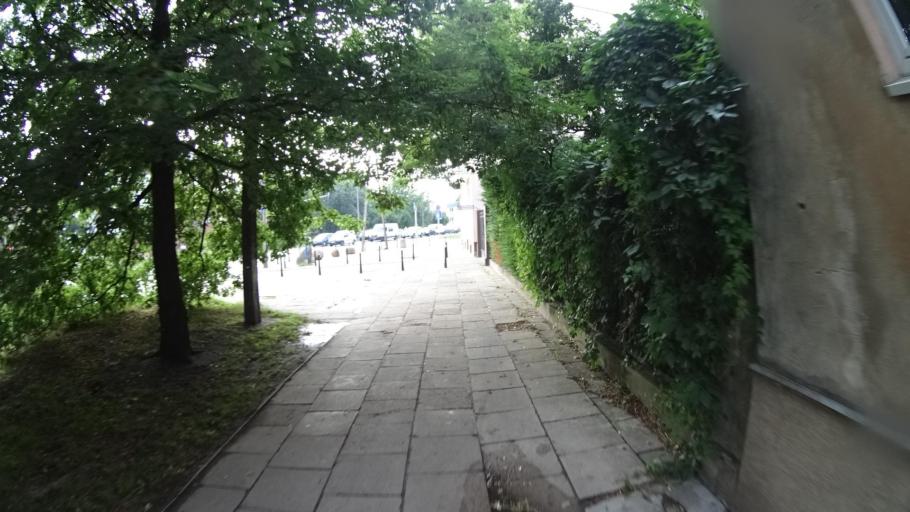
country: PL
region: Masovian Voivodeship
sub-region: Warszawa
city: Ursus
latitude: 52.2091
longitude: 20.9142
